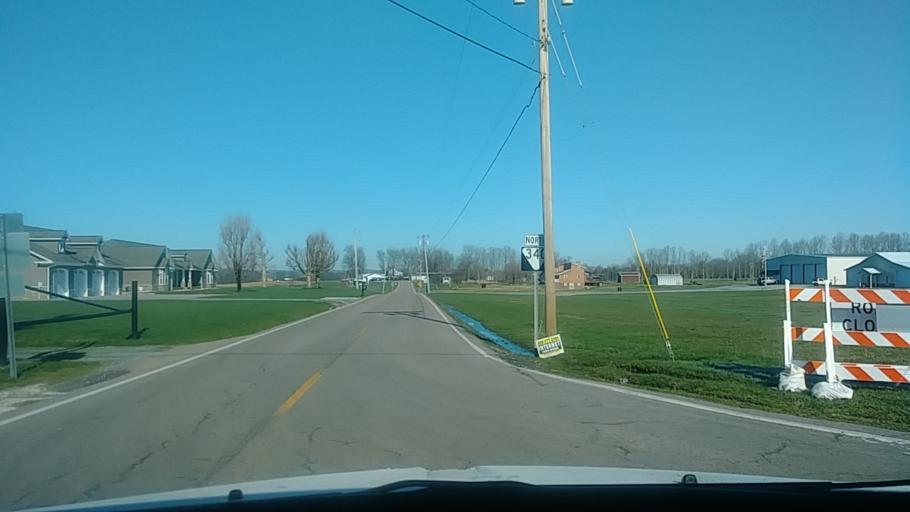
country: US
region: Tennessee
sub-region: Jefferson County
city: White Pine
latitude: 36.1456
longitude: -83.1463
